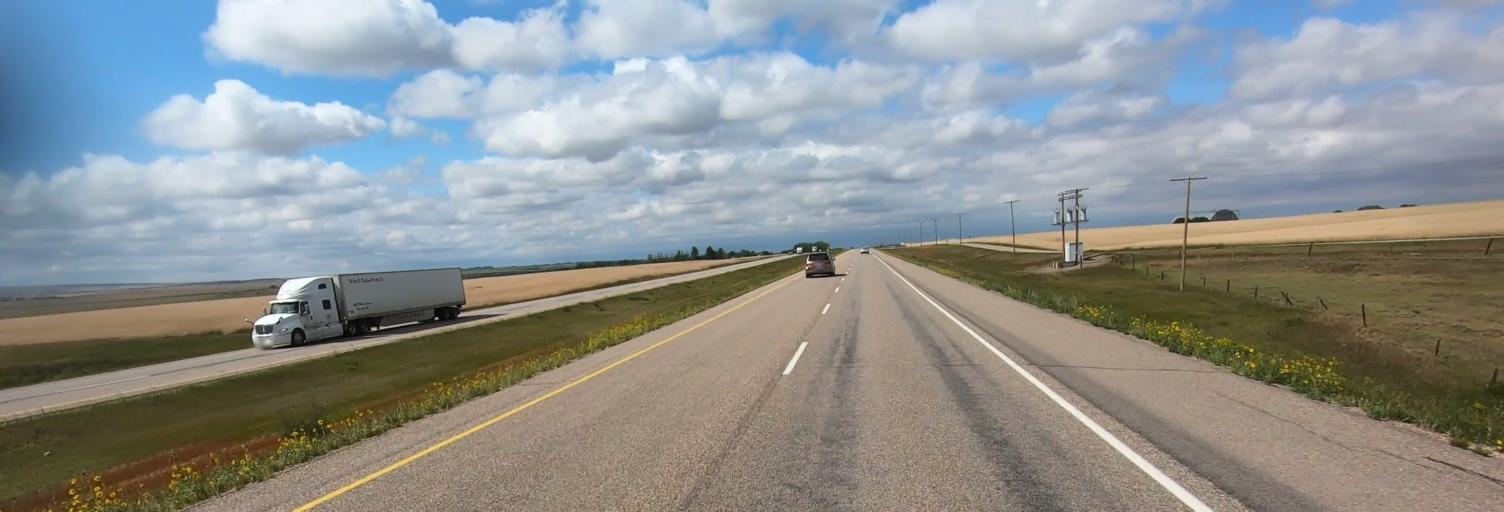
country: CA
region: Saskatchewan
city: Moose Jaw
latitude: 50.4378
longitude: -105.7660
